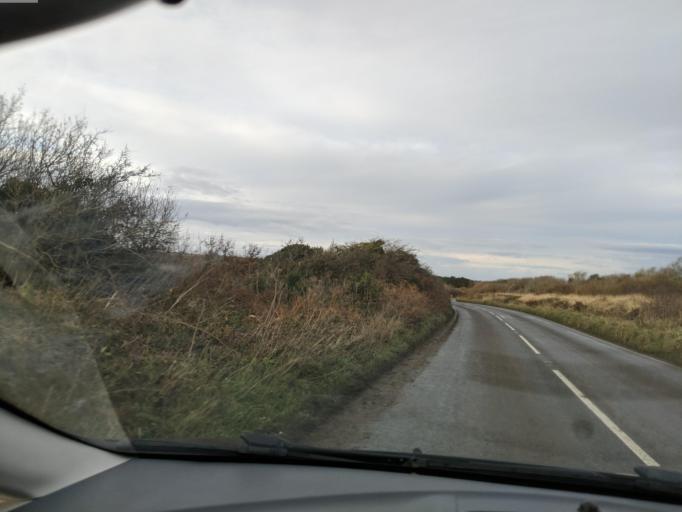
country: GB
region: England
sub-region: Cornwall
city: Jacobstow
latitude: 50.6899
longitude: -4.6156
